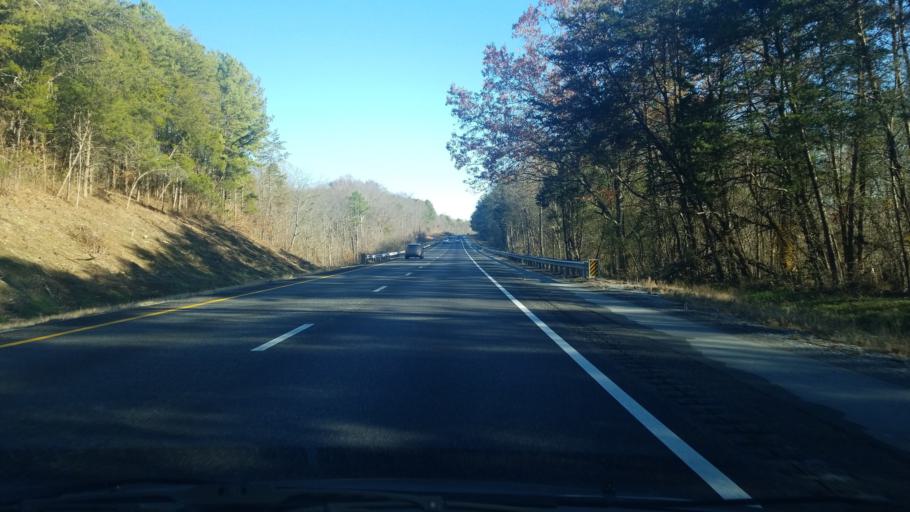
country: US
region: Tennessee
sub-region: Meigs County
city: Decatur
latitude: 35.3806
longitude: -84.7285
